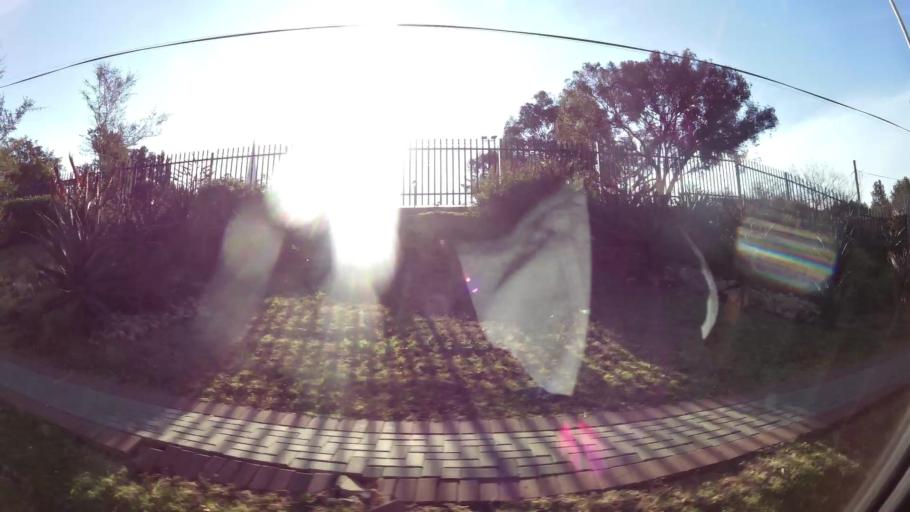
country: ZA
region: Gauteng
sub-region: City of Johannesburg Metropolitan Municipality
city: Roodepoort
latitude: -26.0847
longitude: 27.9407
